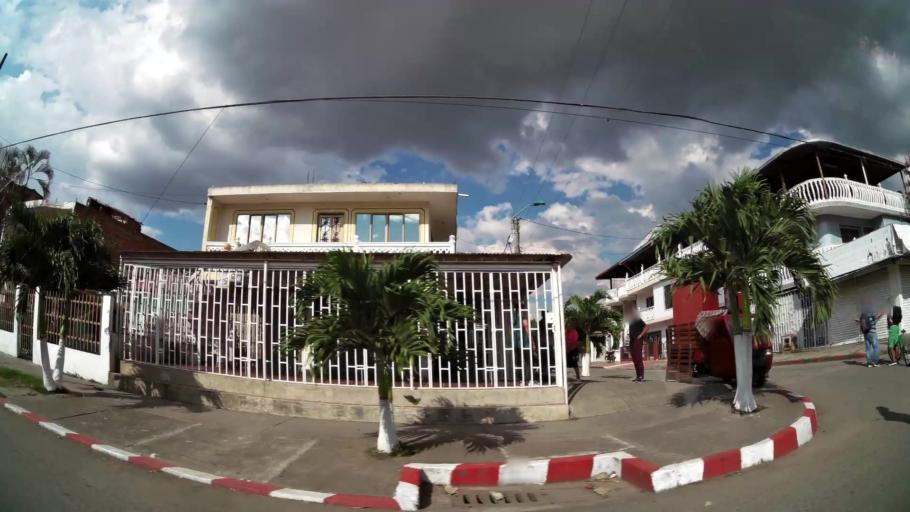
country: CO
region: Valle del Cauca
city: Cali
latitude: 3.4147
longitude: -76.5034
